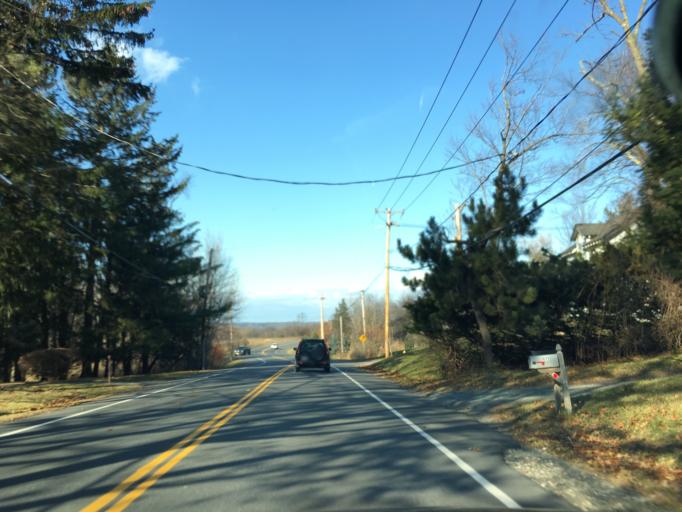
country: US
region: New York
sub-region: Rensselaer County
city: Hampton Manor
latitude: 42.6494
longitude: -73.6891
